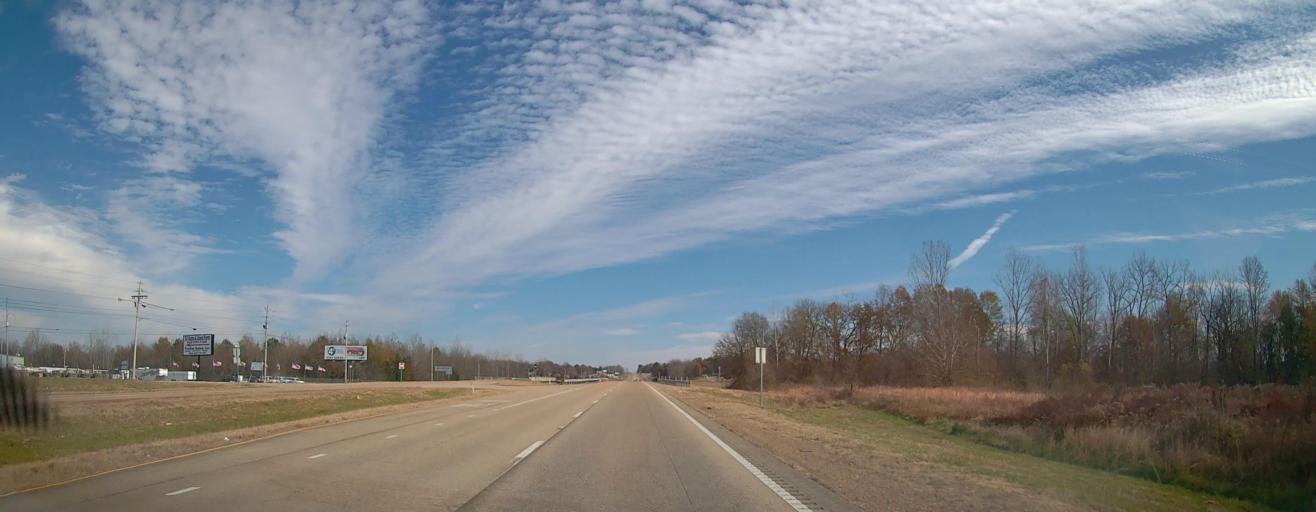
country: US
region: Mississippi
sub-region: Alcorn County
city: Corinth
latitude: 34.9310
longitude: -88.5818
